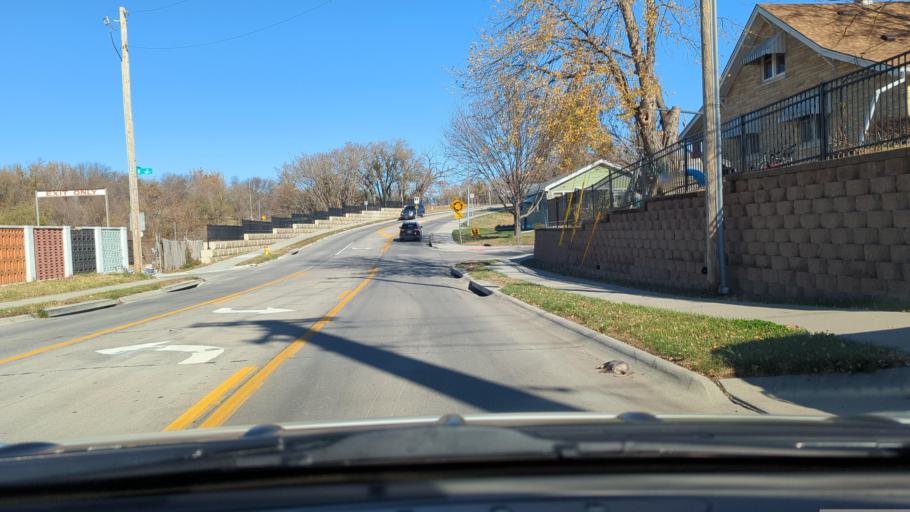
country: US
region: Nebraska
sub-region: Sarpy County
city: La Vista
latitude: 41.2041
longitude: -95.9769
